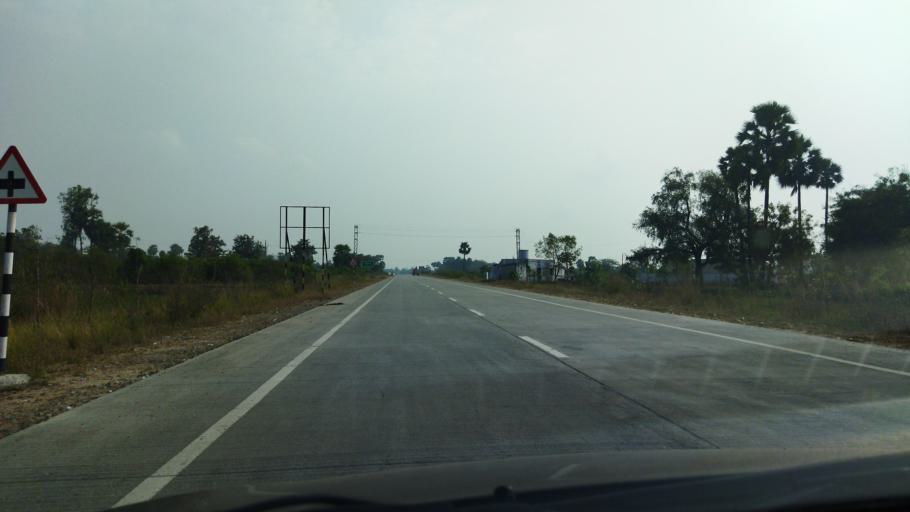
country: IN
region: Telangana
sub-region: Nalgonda
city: Nalgonda
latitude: 17.1813
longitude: 79.4115
